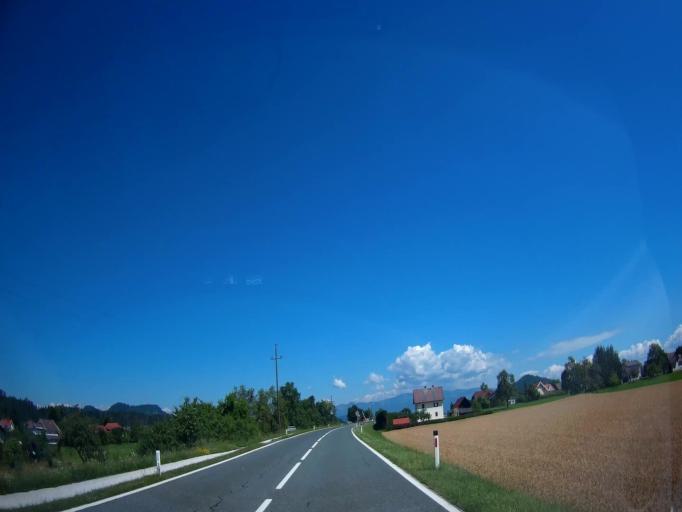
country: AT
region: Carinthia
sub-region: Politischer Bezirk Volkermarkt
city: Eberndorf
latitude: 46.5731
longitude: 14.6305
